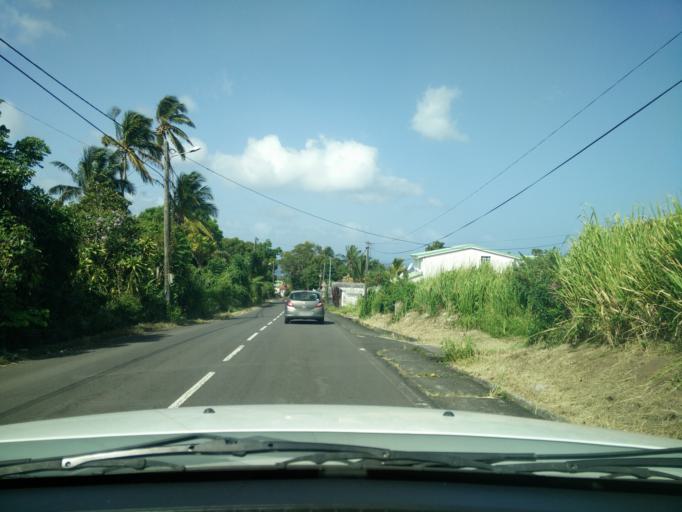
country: GP
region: Guadeloupe
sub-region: Guadeloupe
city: Gourbeyre
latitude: 15.9952
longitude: -61.7051
